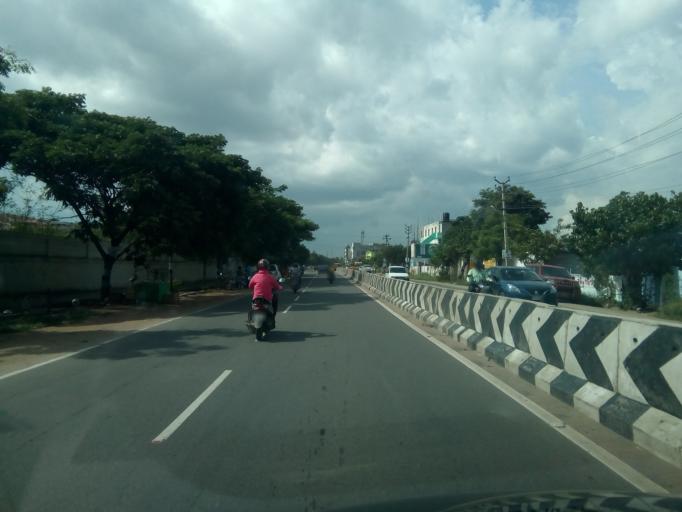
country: IN
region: Tamil Nadu
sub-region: Coimbatore
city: Irugur
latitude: 11.0408
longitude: 77.0377
